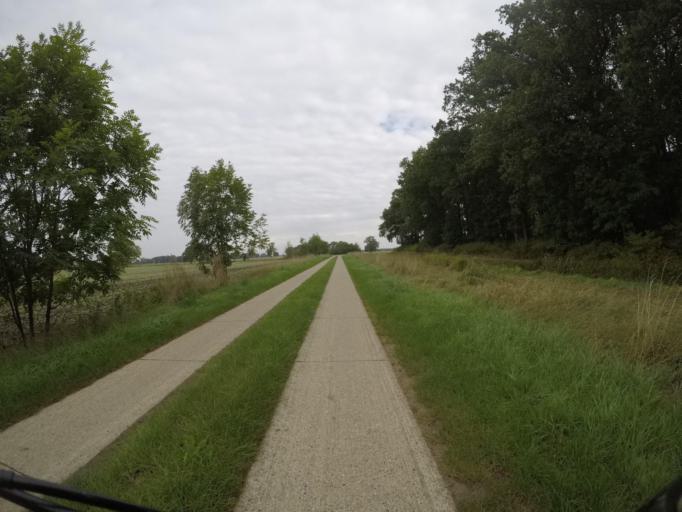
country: DE
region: Lower Saxony
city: Neu Darchau
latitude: 53.2999
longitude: 10.8676
